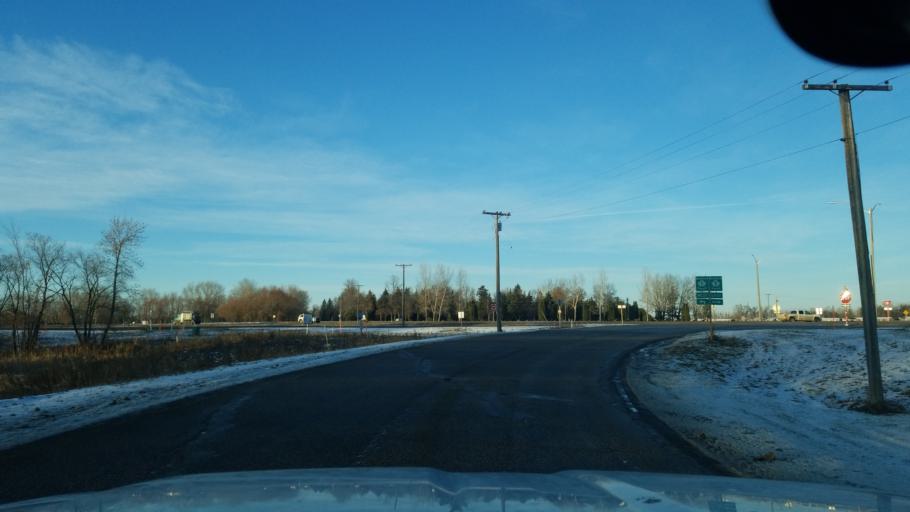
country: CA
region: Manitoba
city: Portage la Prairie
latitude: 49.9539
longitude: -98.3287
